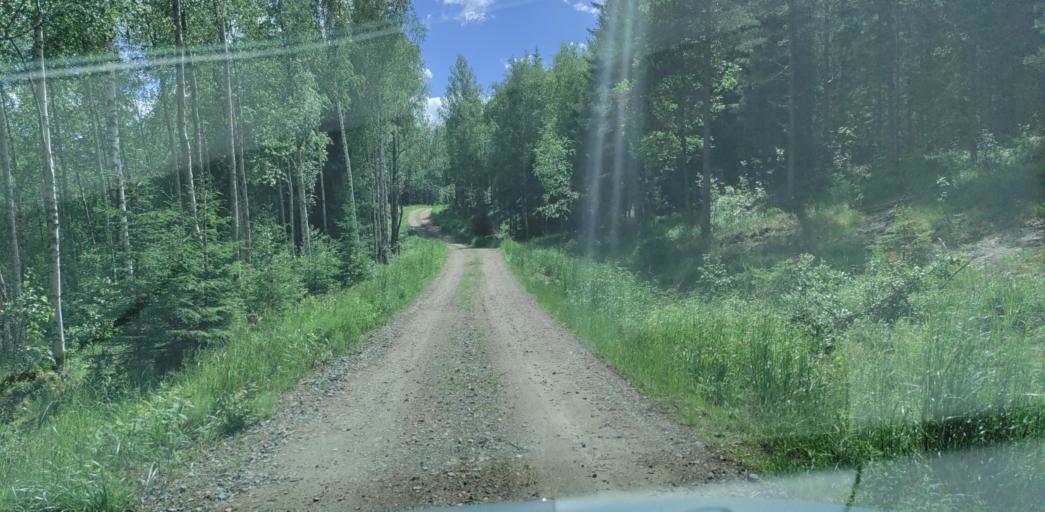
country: SE
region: Vaermland
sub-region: Hagfors Kommun
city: Ekshaerad
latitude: 60.1181
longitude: 13.3256
